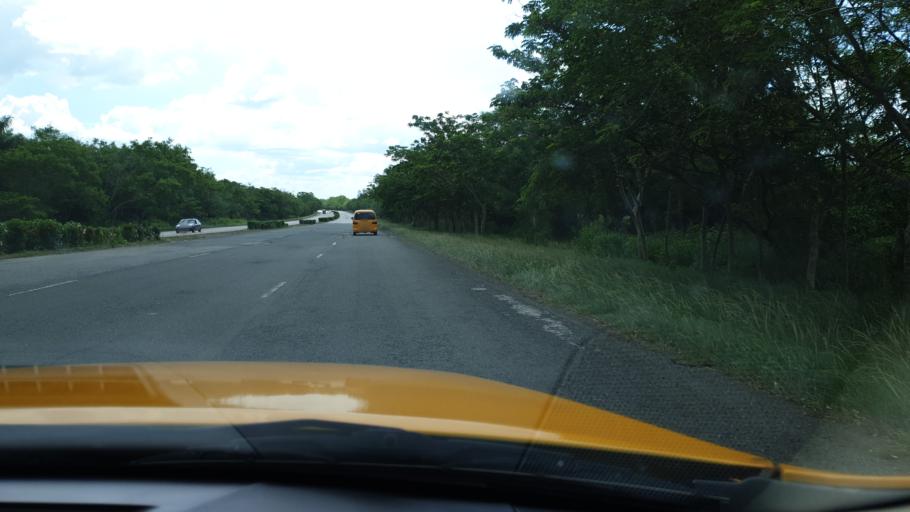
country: CU
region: Cienfuegos
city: Cruces
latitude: 22.4544
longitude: -80.2996
